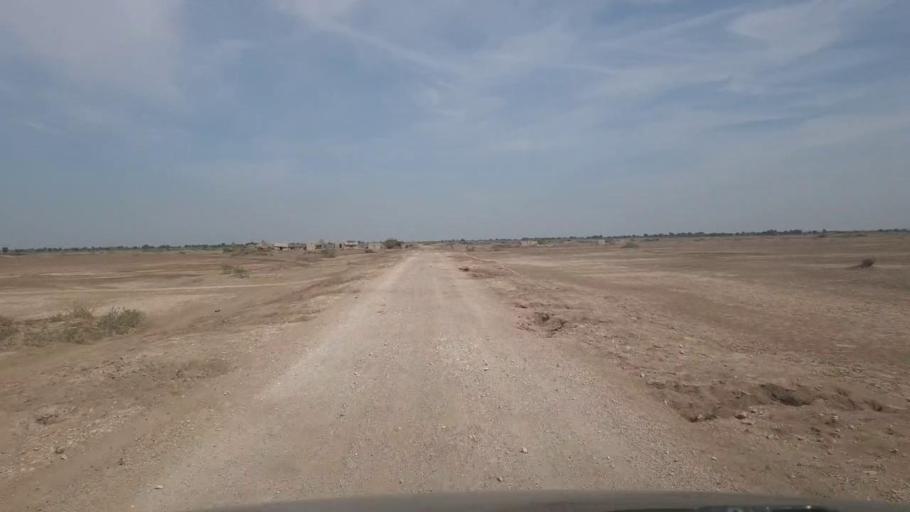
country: PK
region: Sindh
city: Kunri
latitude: 25.2317
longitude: 69.6205
